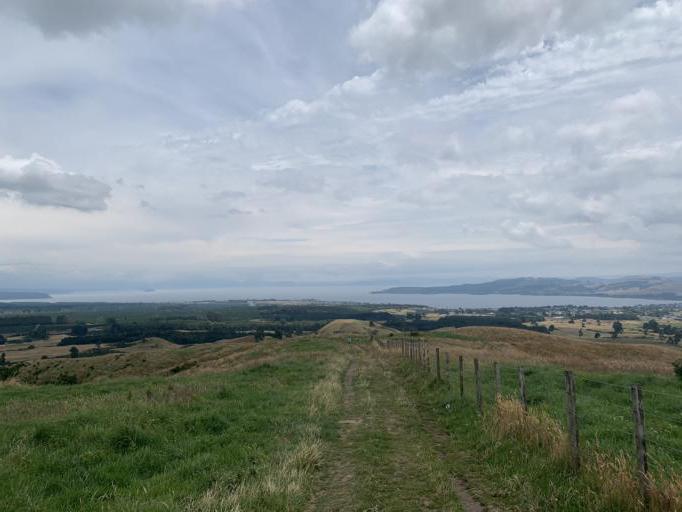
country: NZ
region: Waikato
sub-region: Taupo District
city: Taupo
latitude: -38.6983
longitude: 176.1455
